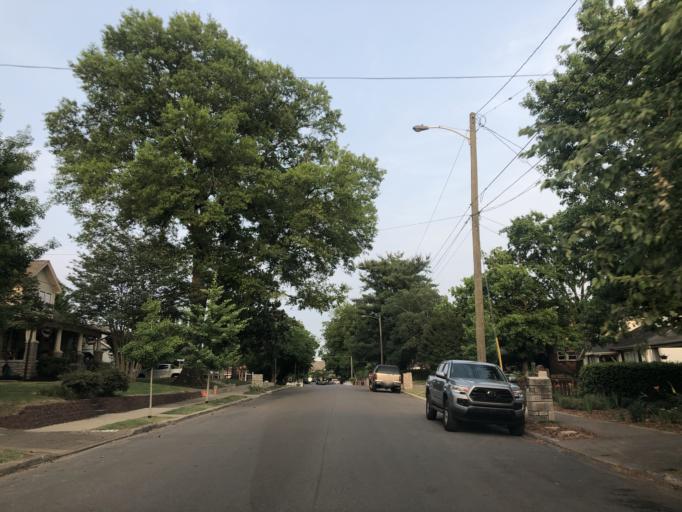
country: US
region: Tennessee
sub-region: Davidson County
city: Nashville
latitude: 36.1277
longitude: -86.7844
